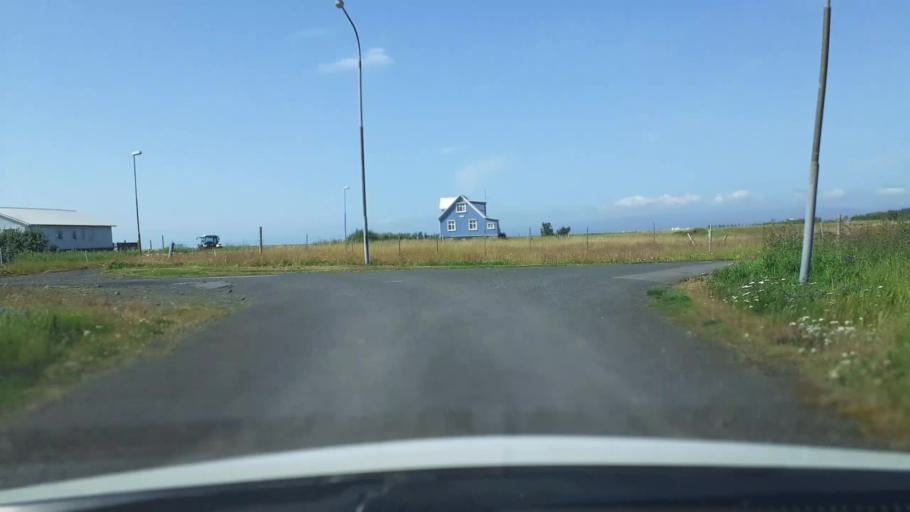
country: IS
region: South
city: Selfoss
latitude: 63.8415
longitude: -21.0522
